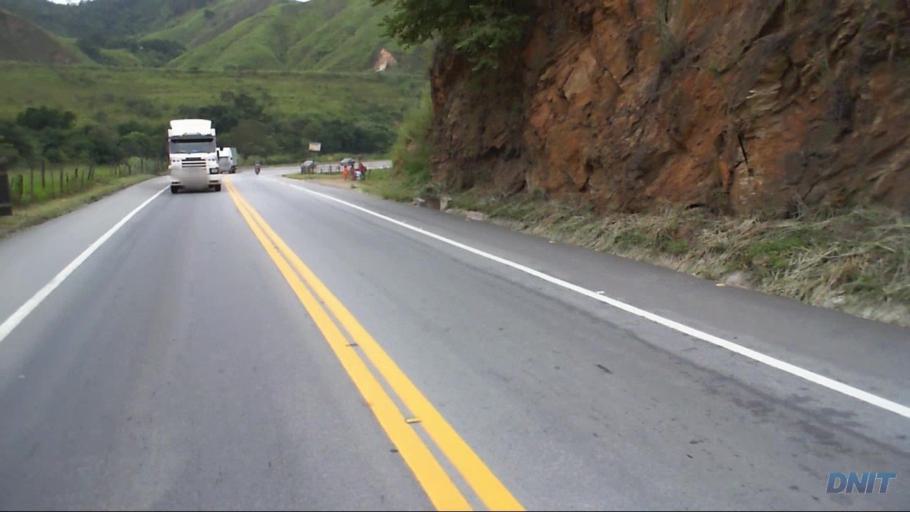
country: BR
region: Minas Gerais
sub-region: Timoteo
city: Timoteo
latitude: -19.6176
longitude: -42.7842
